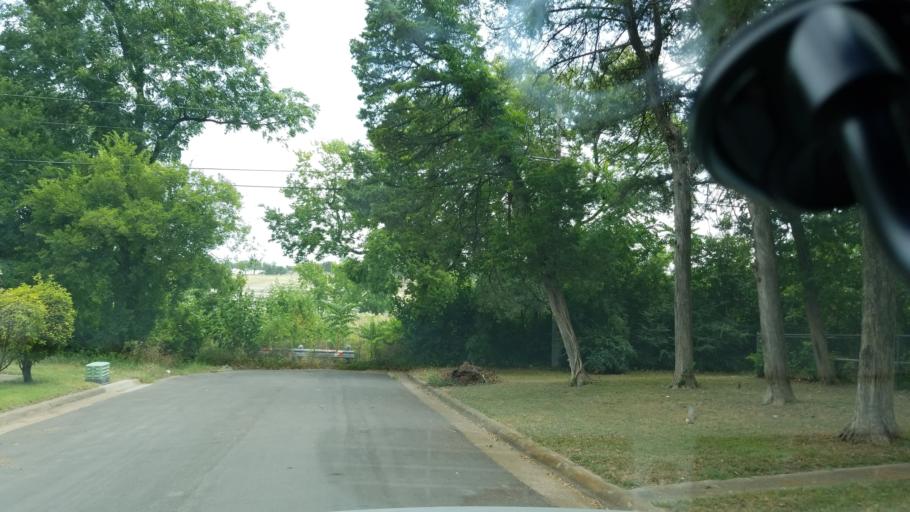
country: US
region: Texas
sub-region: Dallas County
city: Cockrell Hill
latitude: 32.6905
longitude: -96.8489
